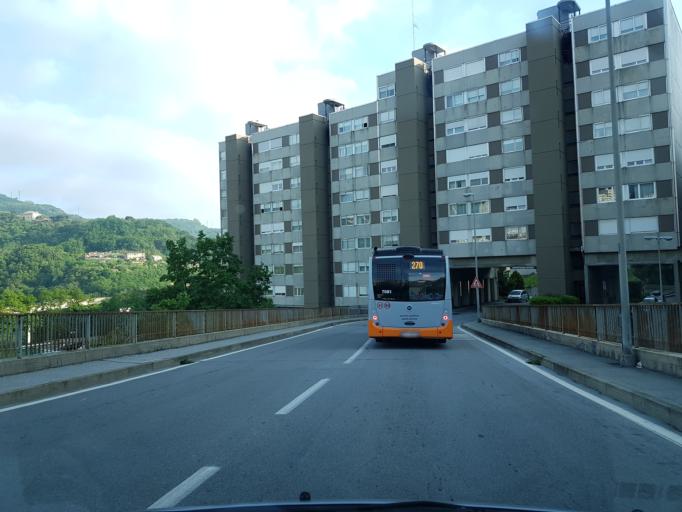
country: IT
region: Liguria
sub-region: Provincia di Genova
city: Genoa
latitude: 44.4450
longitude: 8.9019
